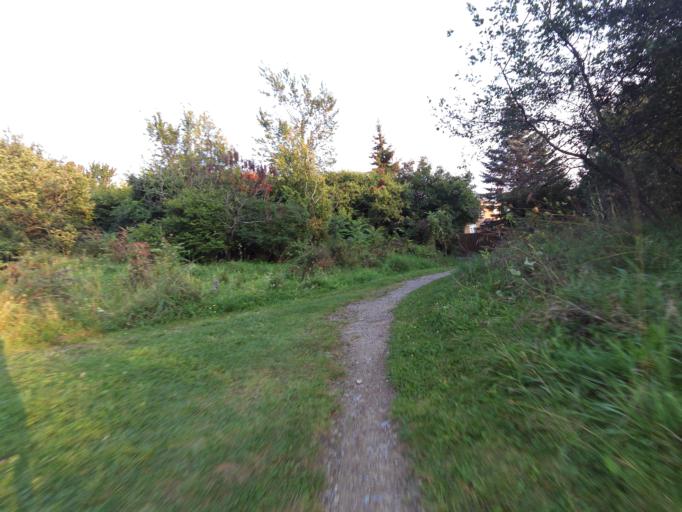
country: CA
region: Ontario
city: Bells Corners
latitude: 45.2880
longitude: -75.8532
